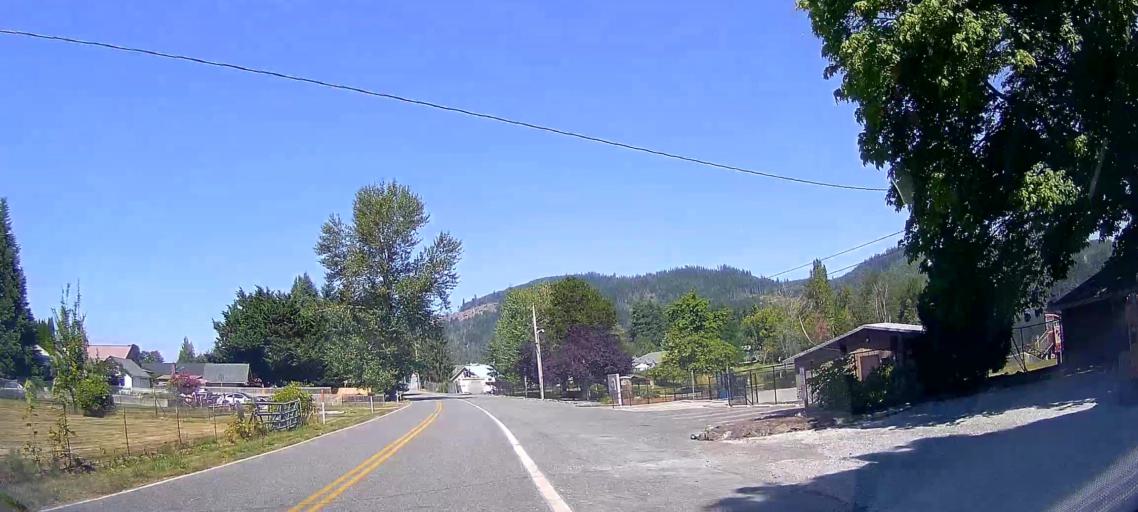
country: US
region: Washington
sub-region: Skagit County
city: Clear Lake
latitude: 48.4578
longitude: -122.2341
